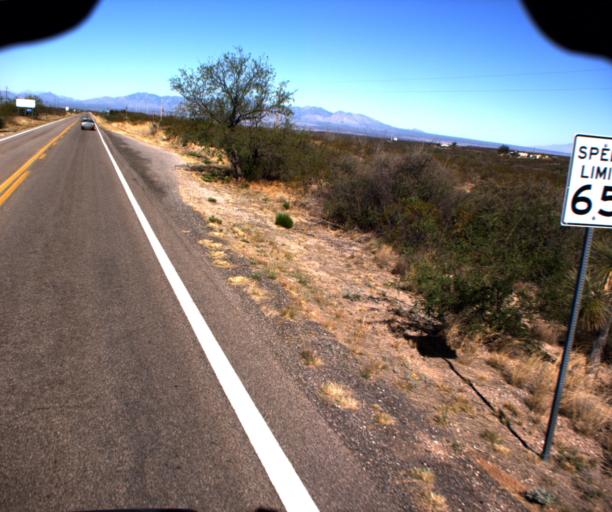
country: US
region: Arizona
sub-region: Cochise County
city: Tombstone
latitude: 31.7481
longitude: -110.0996
